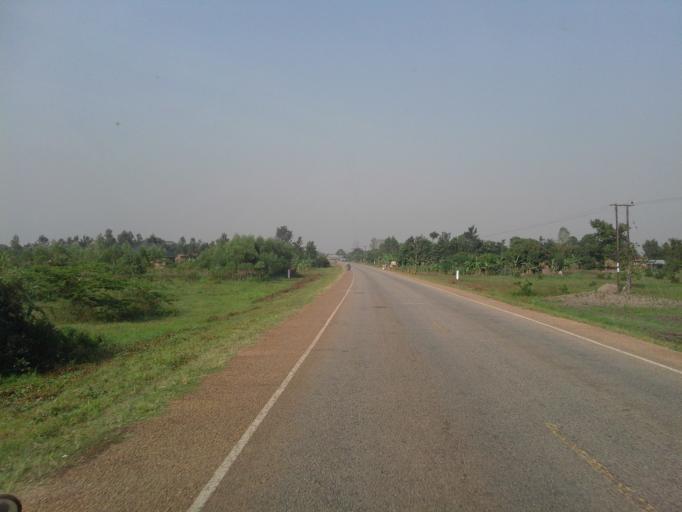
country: UG
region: Eastern Region
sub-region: Mbale District
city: Mbale
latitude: 1.0540
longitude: 34.0566
